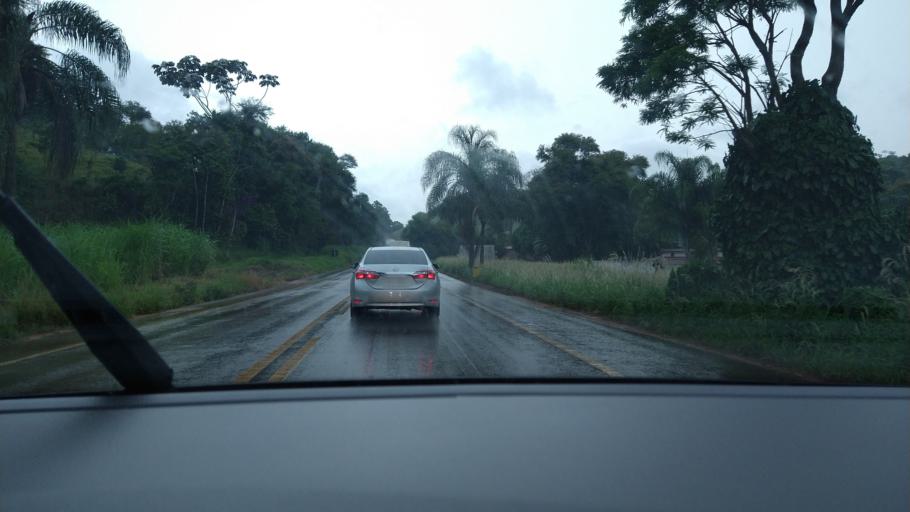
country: BR
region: Minas Gerais
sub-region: Vicosa
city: Vicosa
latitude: -20.6251
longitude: -42.8699
